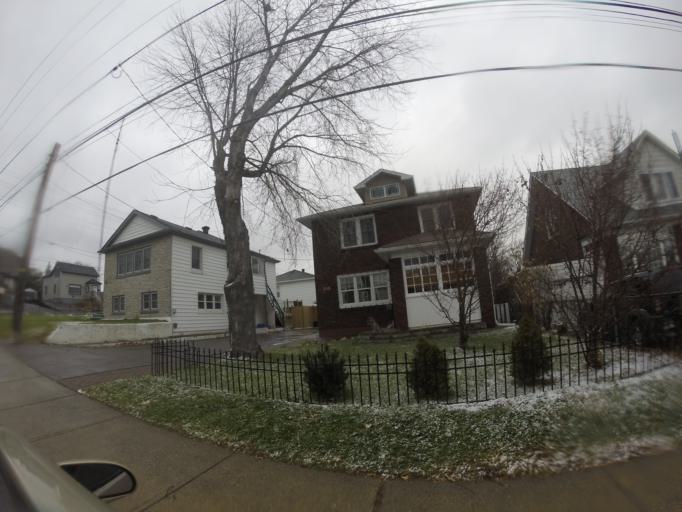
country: CA
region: Ontario
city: Greater Sudbury
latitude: 46.4941
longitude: -81.0068
